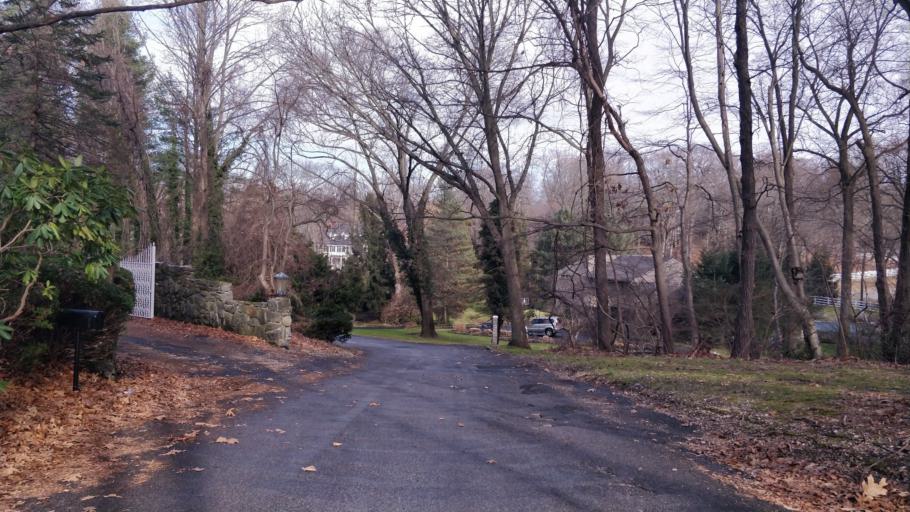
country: US
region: New York
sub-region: Nassau County
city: Oyster Bay
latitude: 40.8726
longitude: -73.5557
